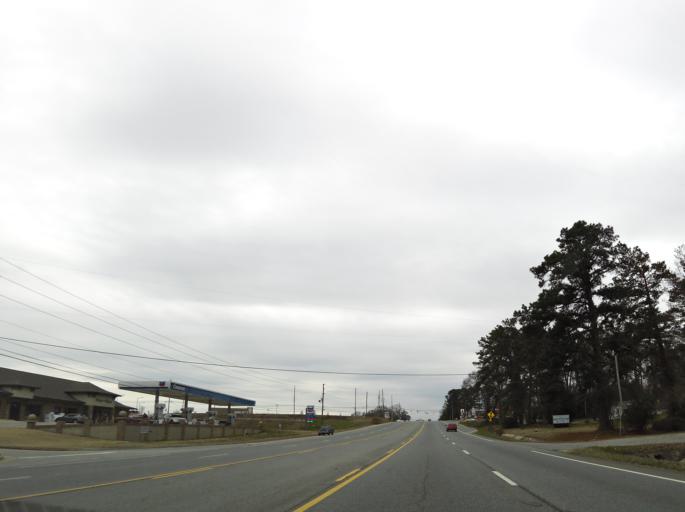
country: US
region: Georgia
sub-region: Houston County
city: Robins Air Force Base
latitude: 32.5709
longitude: -83.5930
